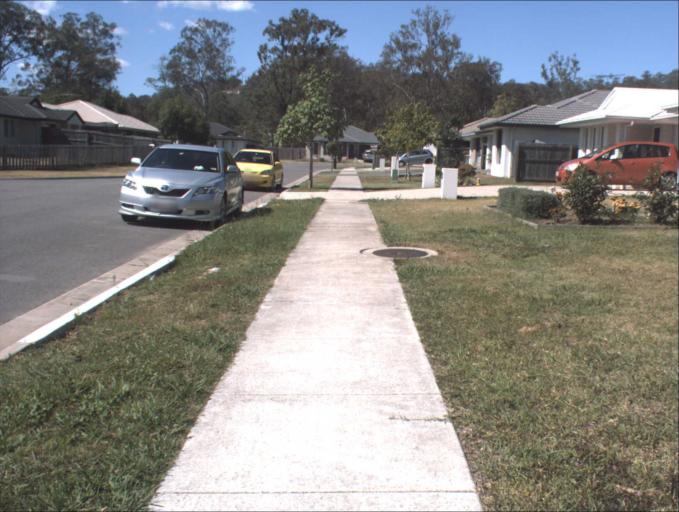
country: AU
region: Queensland
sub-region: Logan
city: Windaroo
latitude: -27.7575
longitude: 153.1866
